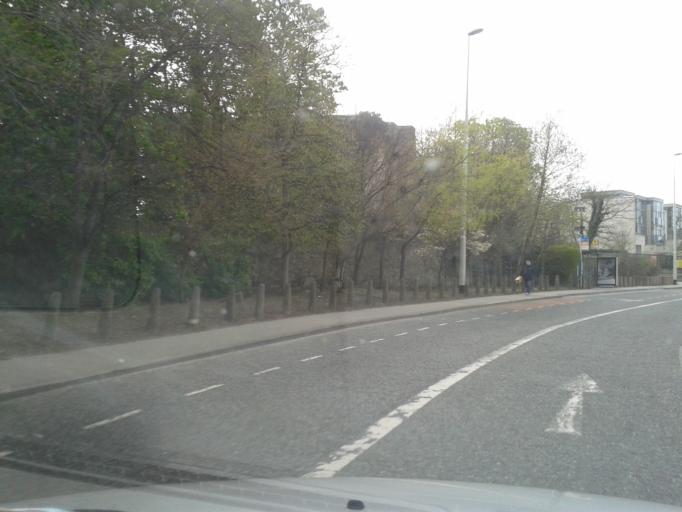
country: IE
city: Booterstown
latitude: 53.3077
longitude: -6.1943
